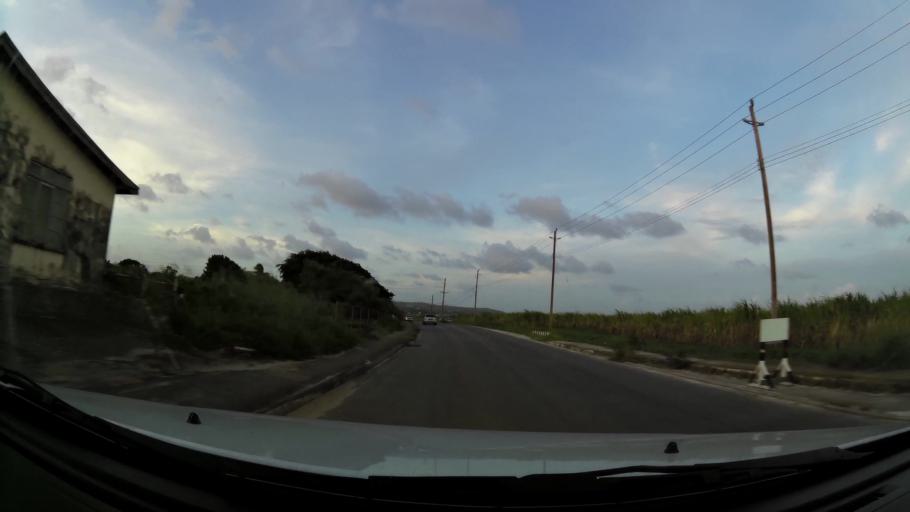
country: BB
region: Saint Philip
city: Crane
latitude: 13.1080
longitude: -59.4849
